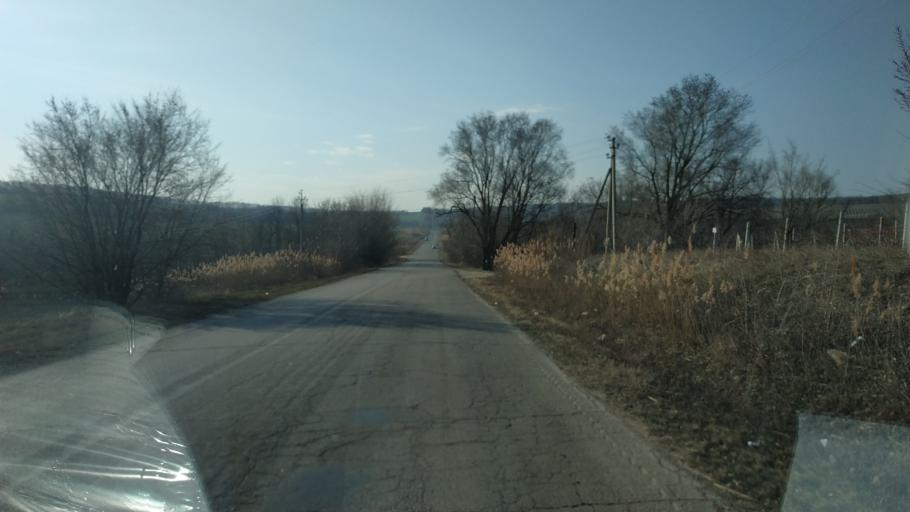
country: MD
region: Chisinau
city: Singera
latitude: 46.8885
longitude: 29.0391
